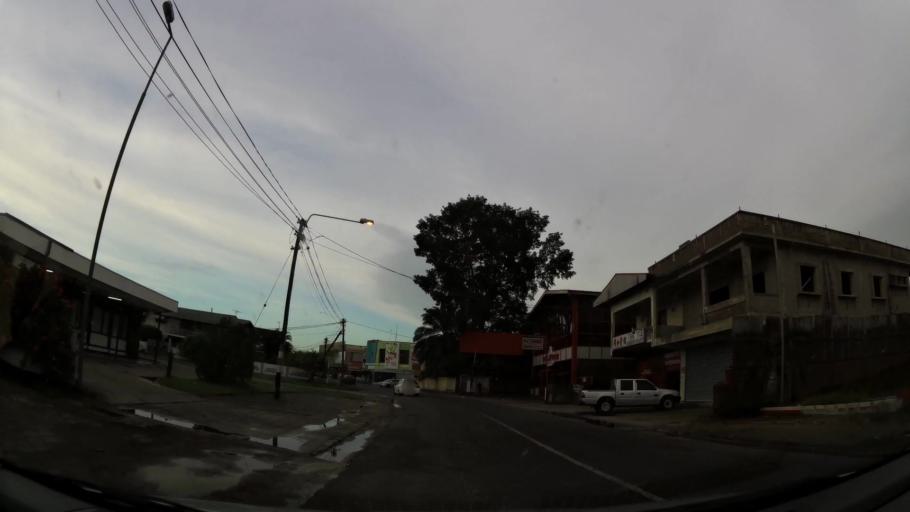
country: SR
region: Paramaribo
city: Paramaribo
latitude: 5.8276
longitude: -55.1920
